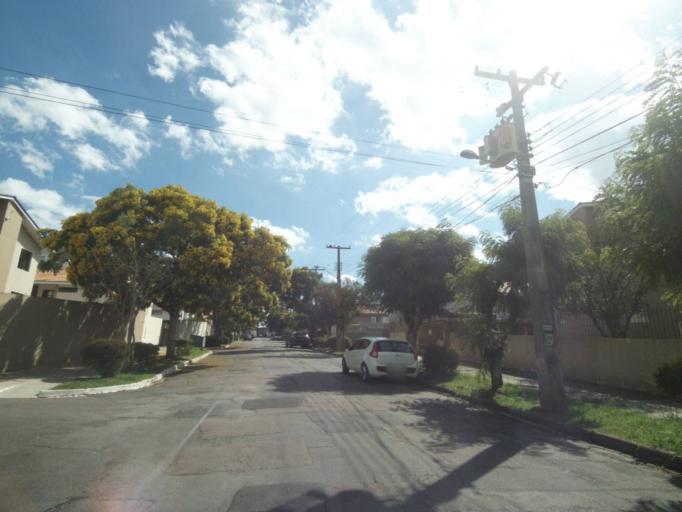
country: BR
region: Parana
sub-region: Curitiba
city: Curitiba
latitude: -25.4374
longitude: -49.3458
